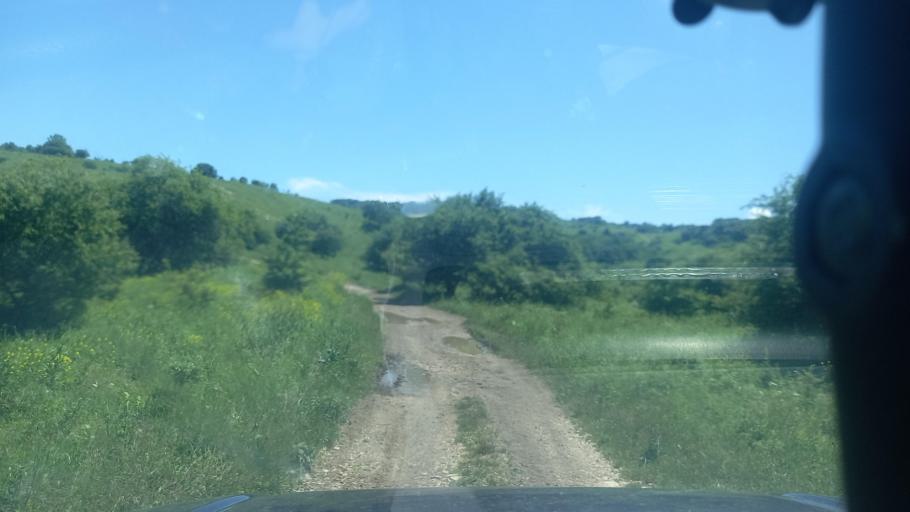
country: RU
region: Karachayevo-Cherkesiya
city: Pregradnaya
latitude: 44.1027
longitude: 41.1190
